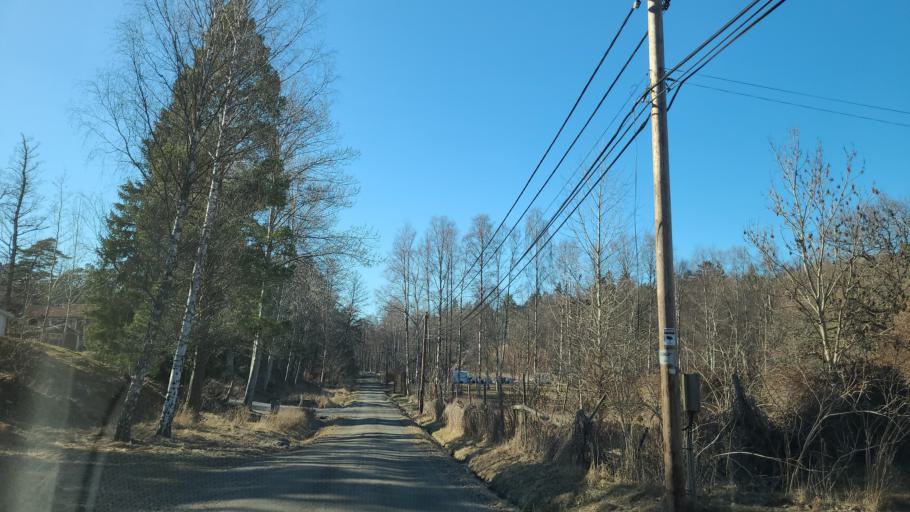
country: SE
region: Stockholm
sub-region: Varmdo Kommun
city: Holo
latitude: 59.3627
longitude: 18.6636
